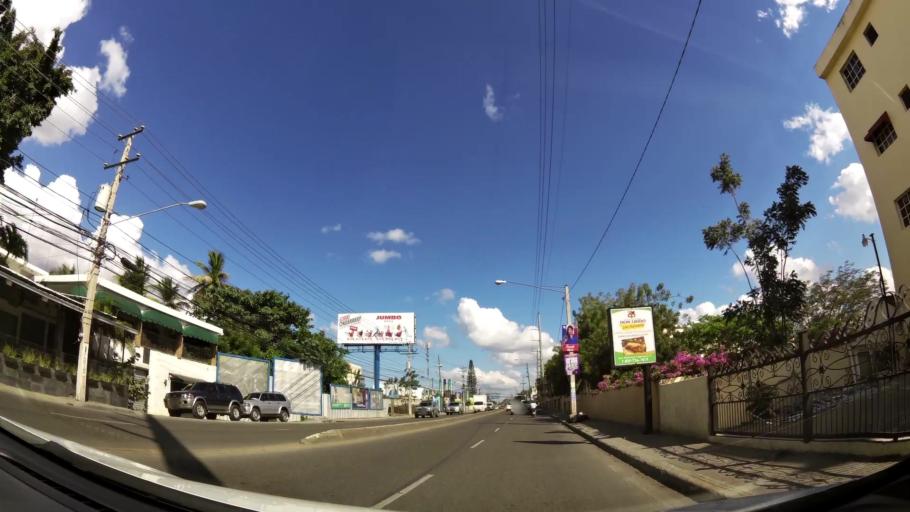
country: DO
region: Santiago
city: Santiago de los Caballeros
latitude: 19.4571
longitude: -70.6673
